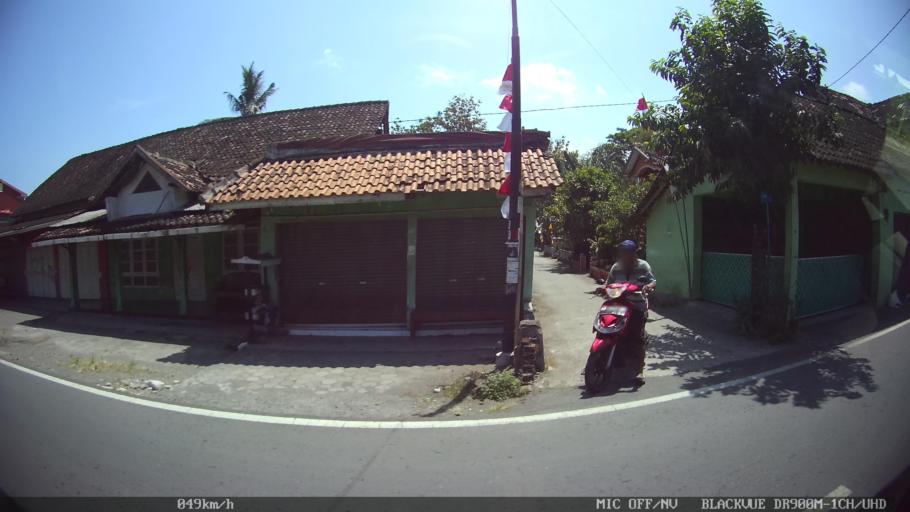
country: ID
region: Daerah Istimewa Yogyakarta
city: Srandakan
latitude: -7.9383
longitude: 110.2541
